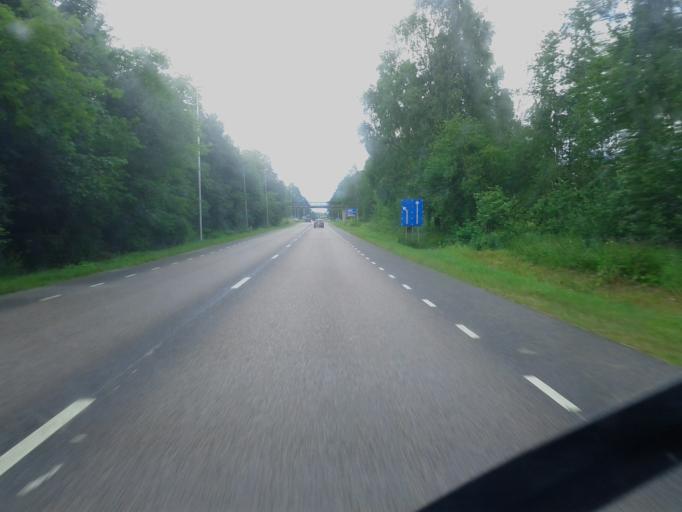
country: SE
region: Vaestmanland
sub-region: Sala Kommun
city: Sala
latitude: 59.9123
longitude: 16.5870
